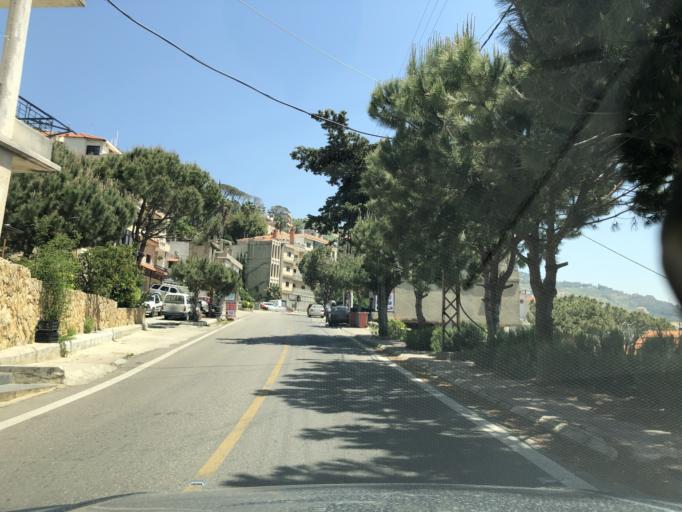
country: LB
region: Mont-Liban
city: Beit ed Dine
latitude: 33.6889
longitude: 35.5279
